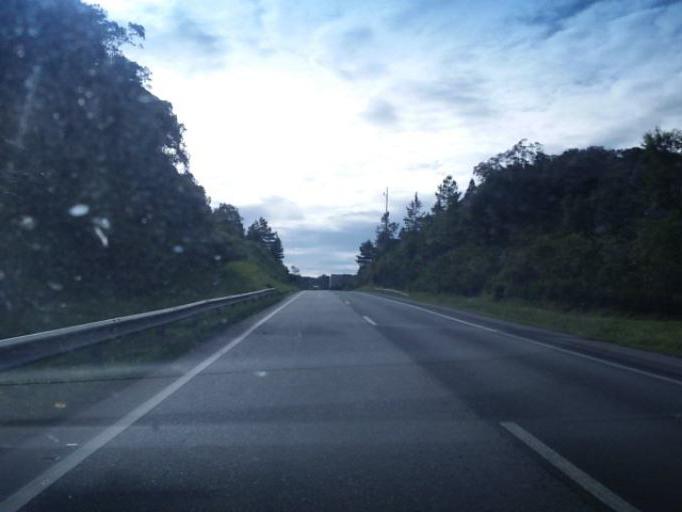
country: BR
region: Parana
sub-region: Antonina
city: Antonina
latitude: -25.1072
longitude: -48.7822
